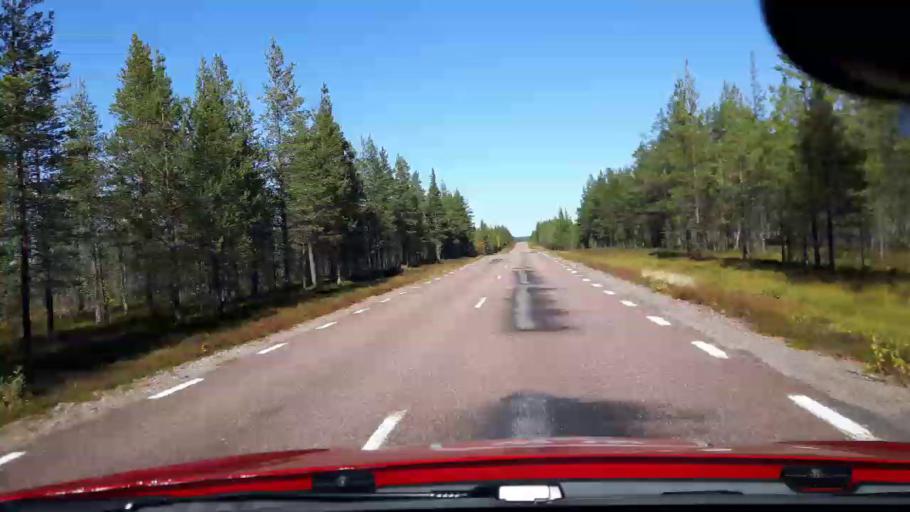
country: SE
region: Jaemtland
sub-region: Harjedalens Kommun
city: Sveg
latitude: 61.7481
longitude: 14.1569
